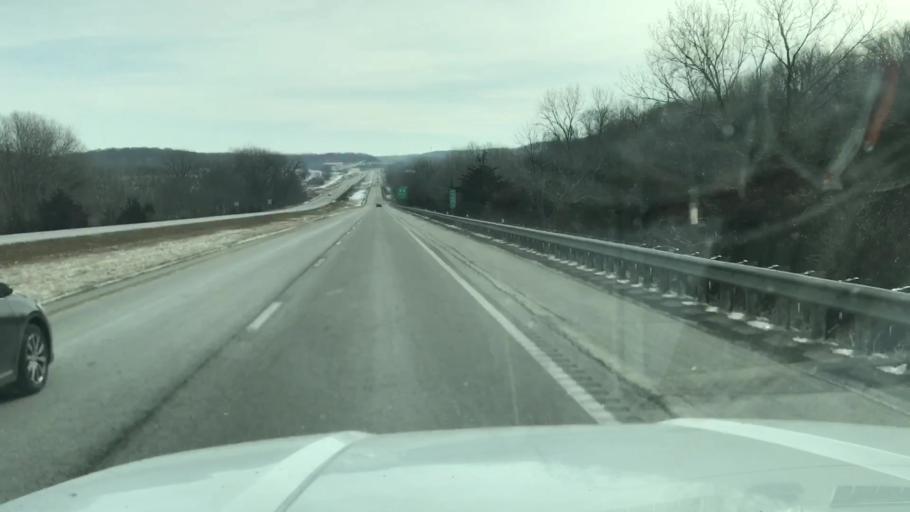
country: US
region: Missouri
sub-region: Holt County
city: Oregon
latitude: 39.9725
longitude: -95.0025
